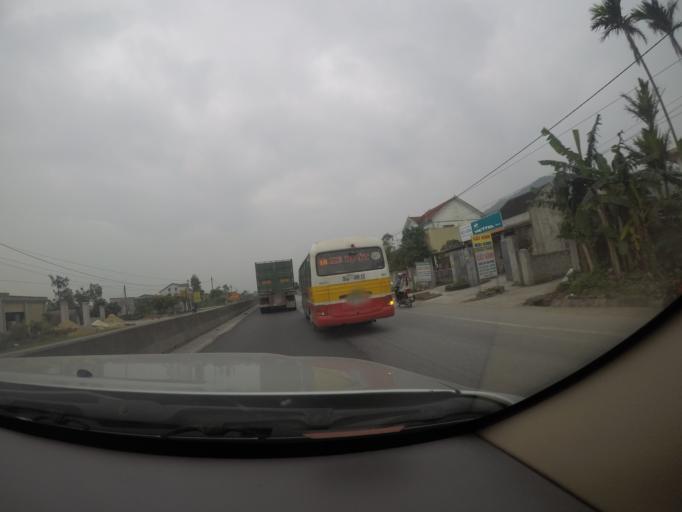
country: VN
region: Ha Tinh
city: Ky Anh
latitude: 18.1366
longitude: 106.2529
